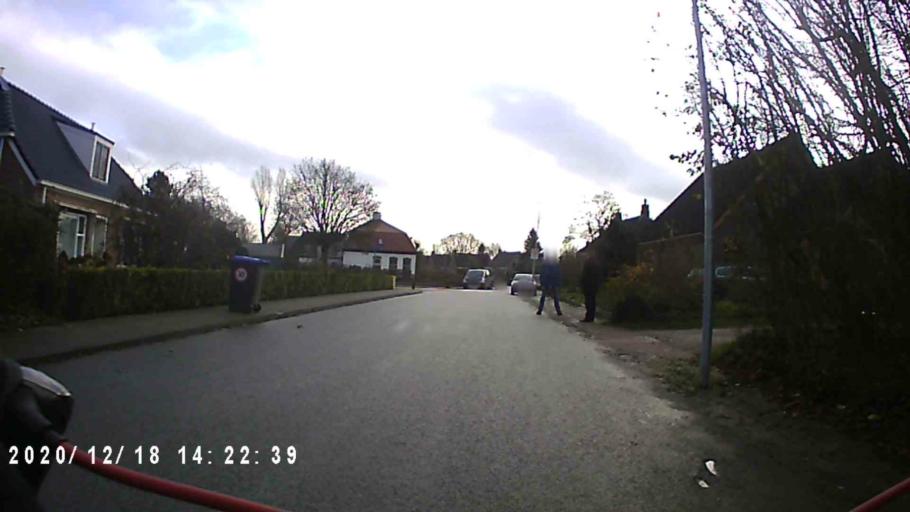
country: NL
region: Groningen
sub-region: Gemeente Groningen
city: Oosterpark
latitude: 53.2480
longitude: 6.6481
